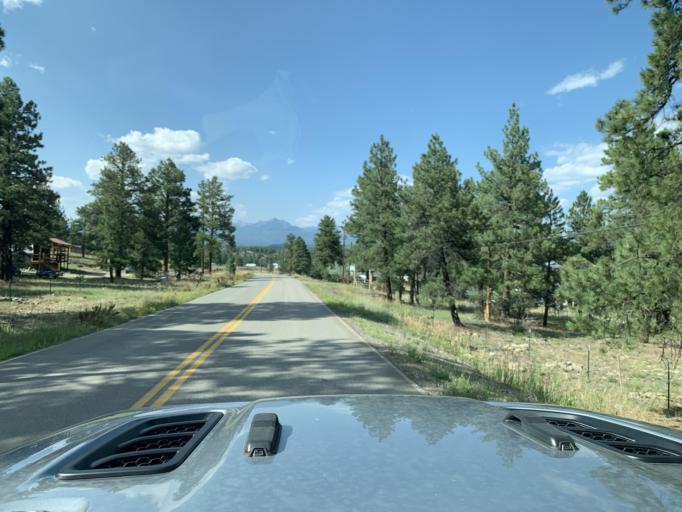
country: US
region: Colorado
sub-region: Archuleta County
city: Pagosa Springs
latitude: 37.2493
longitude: -107.0249
